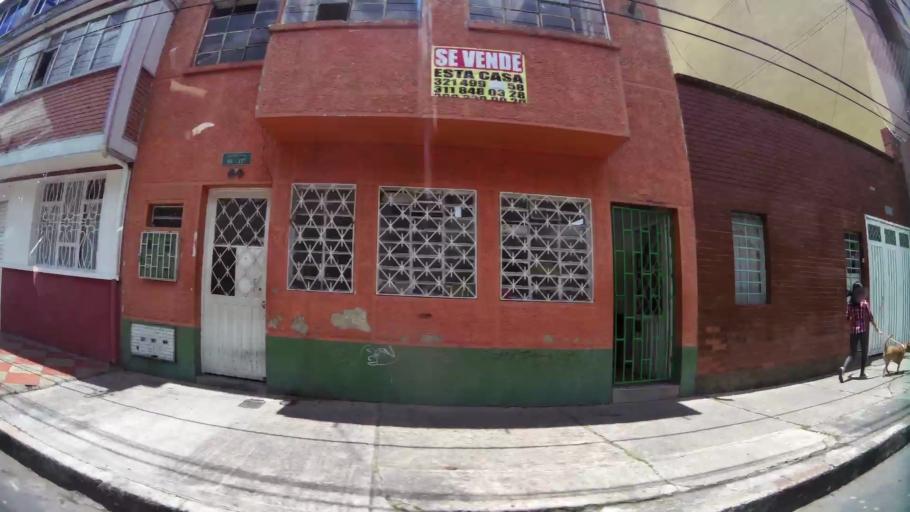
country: CO
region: Bogota D.C.
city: Bogota
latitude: 4.5918
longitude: -74.1032
